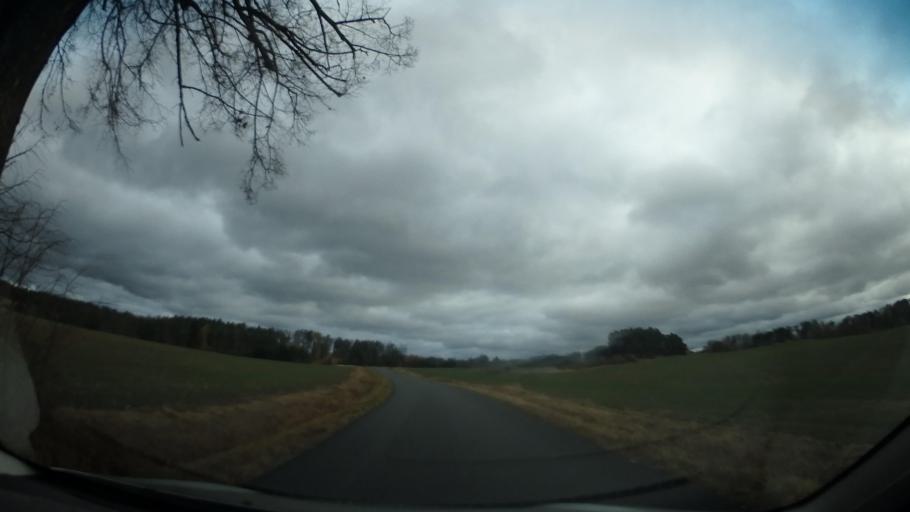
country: CZ
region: Vysocina
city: Namest' nad Oslavou
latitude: 49.2870
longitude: 16.1102
